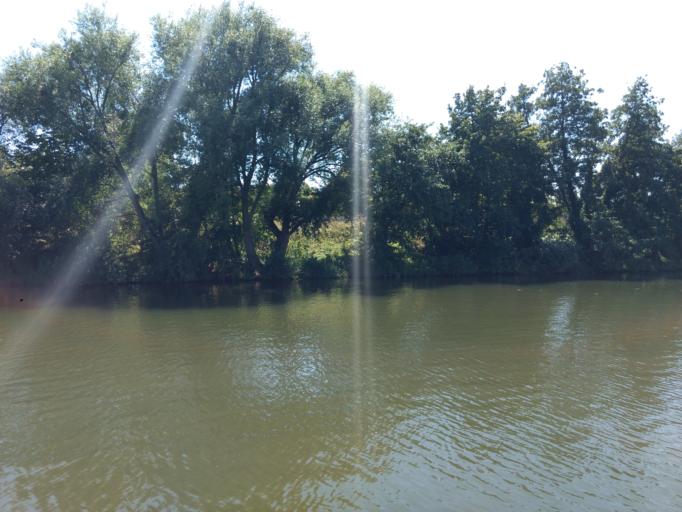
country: DE
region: Bavaria
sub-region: Upper Franconia
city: Hallstadt
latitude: 49.9069
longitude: 10.8630
